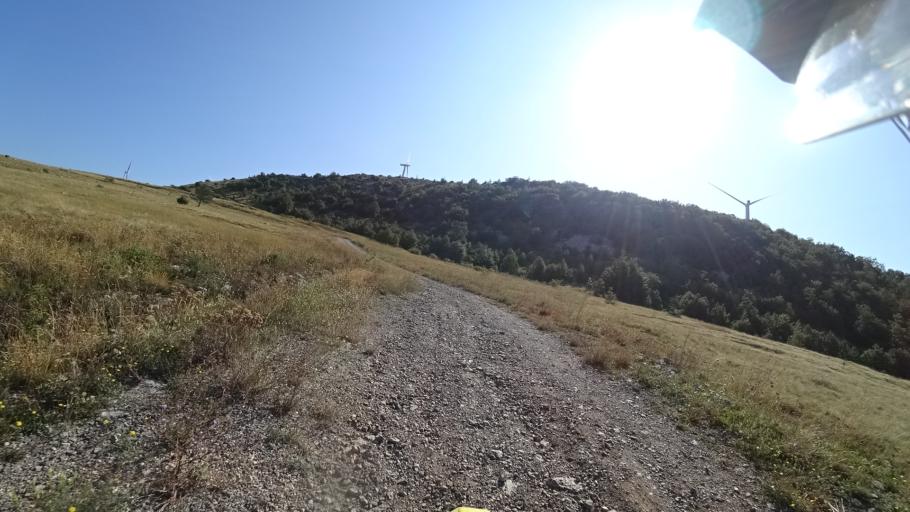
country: HR
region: Zadarska
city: Gracac
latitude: 44.2593
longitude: 16.0758
